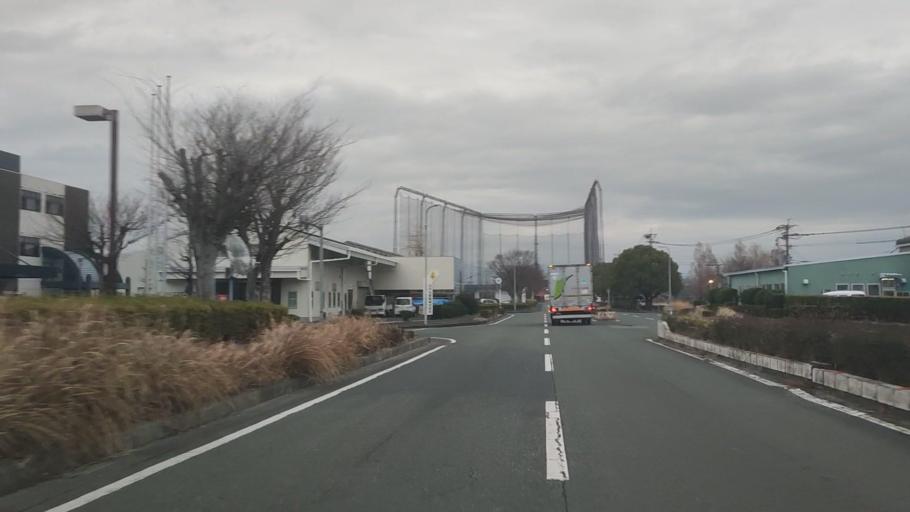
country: JP
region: Kumamoto
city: Kumamoto
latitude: 32.7669
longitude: 130.7068
